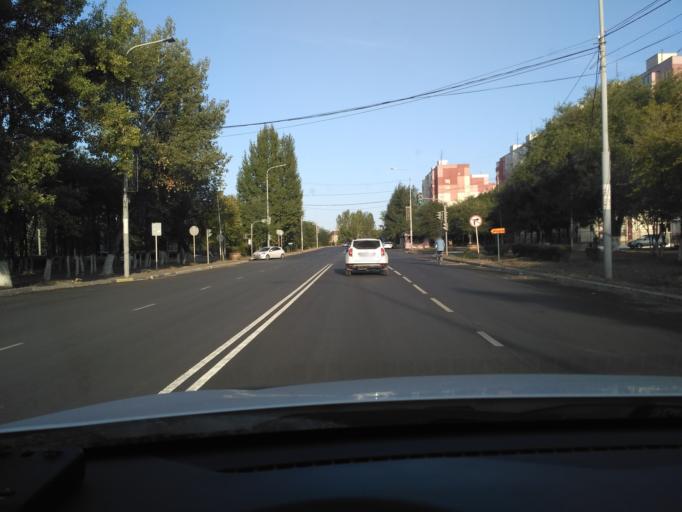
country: KZ
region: Batys Qazaqstan
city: Aqsay
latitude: 51.1657
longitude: 53.0276
